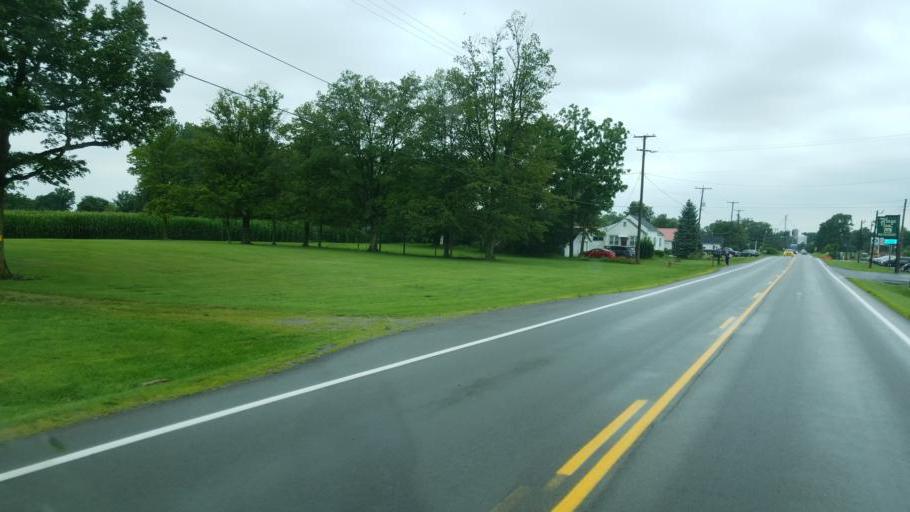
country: US
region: Ohio
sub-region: Hardin County
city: Kenton
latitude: 40.5275
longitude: -83.5160
